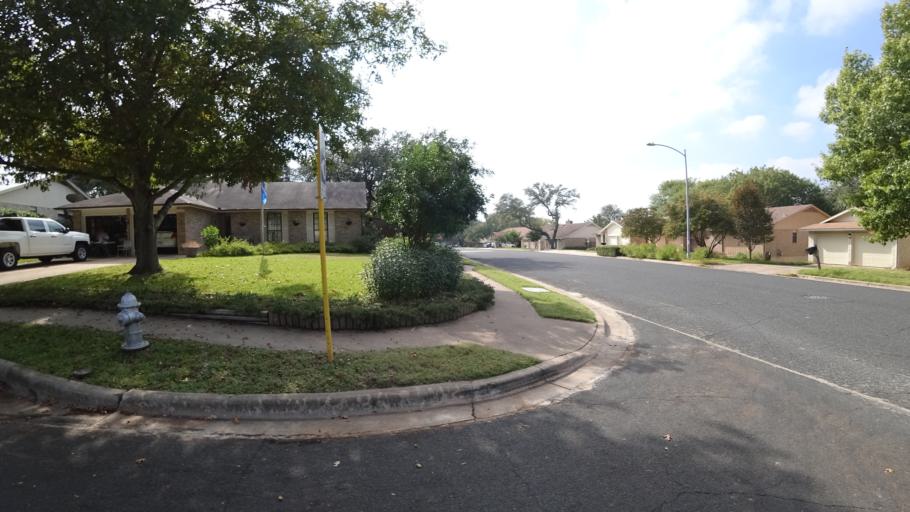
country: US
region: Texas
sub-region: Travis County
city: Shady Hollow
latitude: 30.1999
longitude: -97.8189
